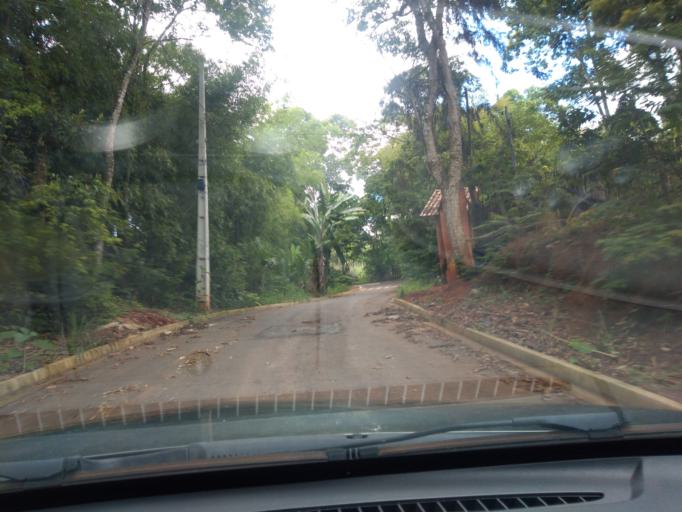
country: BR
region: Minas Gerais
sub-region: Tres Coracoes
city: Tres Coracoes
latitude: -21.6866
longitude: -45.2698
